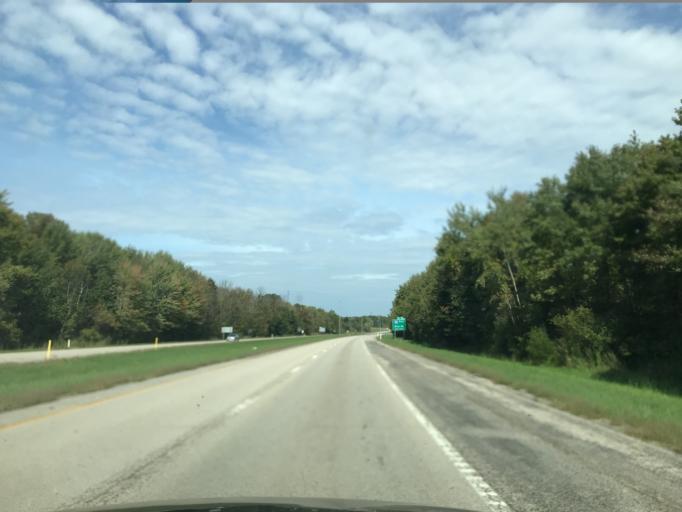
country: US
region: Ohio
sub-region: Ashtabula County
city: Ashtabula
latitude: 41.8161
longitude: -80.7628
